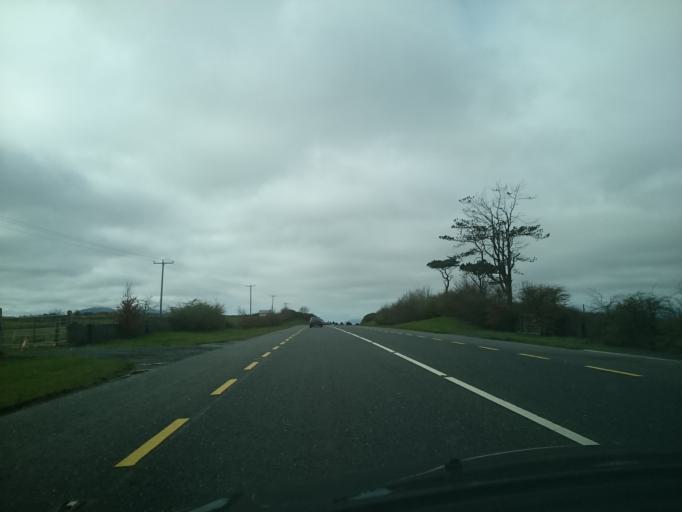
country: IE
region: Connaught
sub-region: Maigh Eo
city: Westport
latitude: 53.8032
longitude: -9.4774
